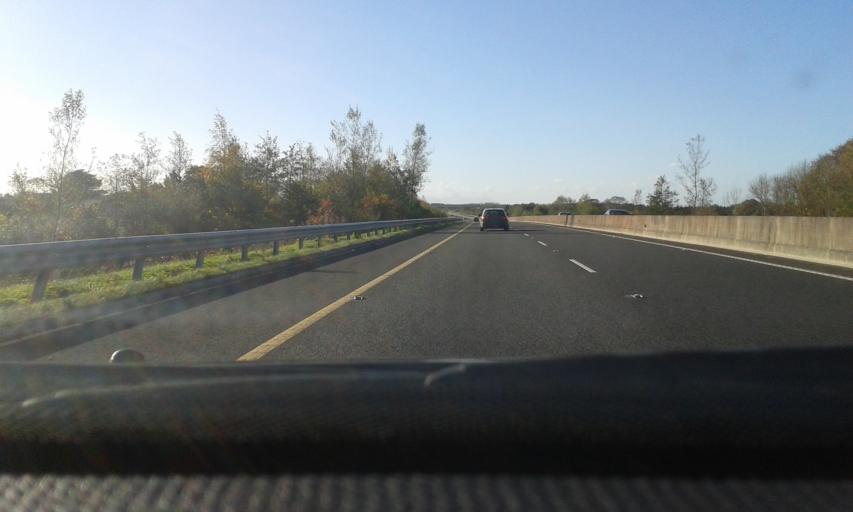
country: IE
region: Munster
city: Thurles
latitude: 52.6907
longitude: -7.6656
